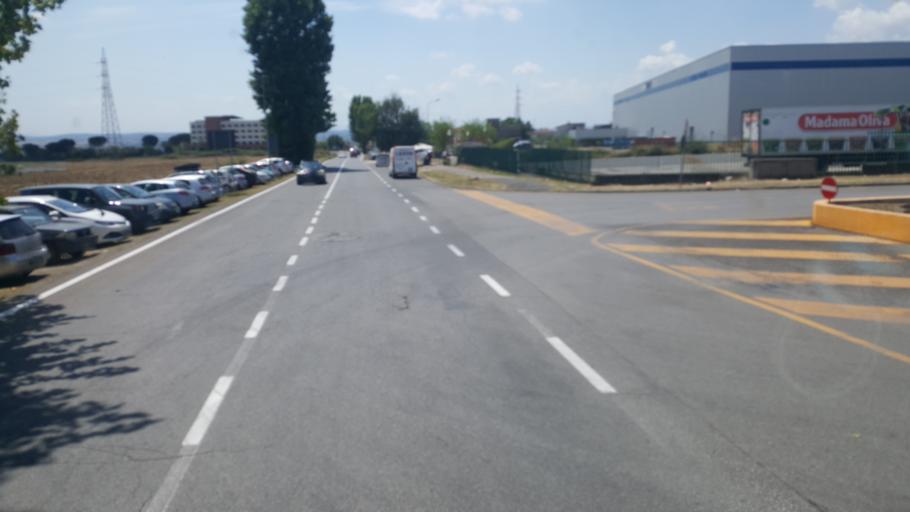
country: IT
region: Latium
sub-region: Citta metropolitana di Roma Capitale
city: Fiano Romano
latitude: 42.1393
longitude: 12.5965
